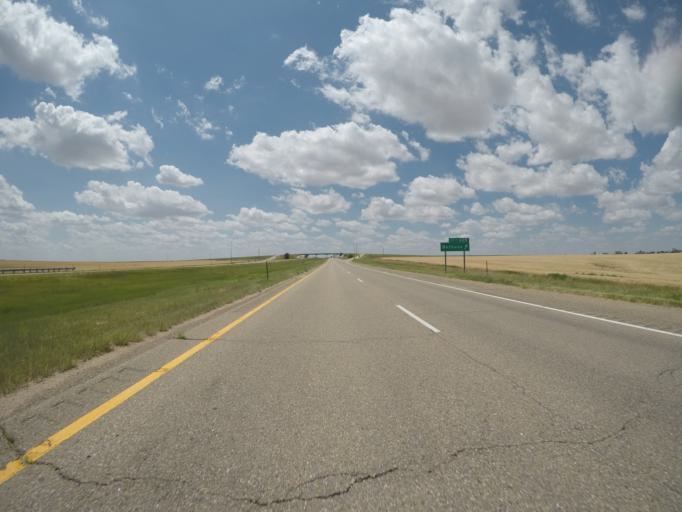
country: US
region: Colorado
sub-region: Kit Carson County
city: Burlington
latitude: 39.2942
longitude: -102.4222
